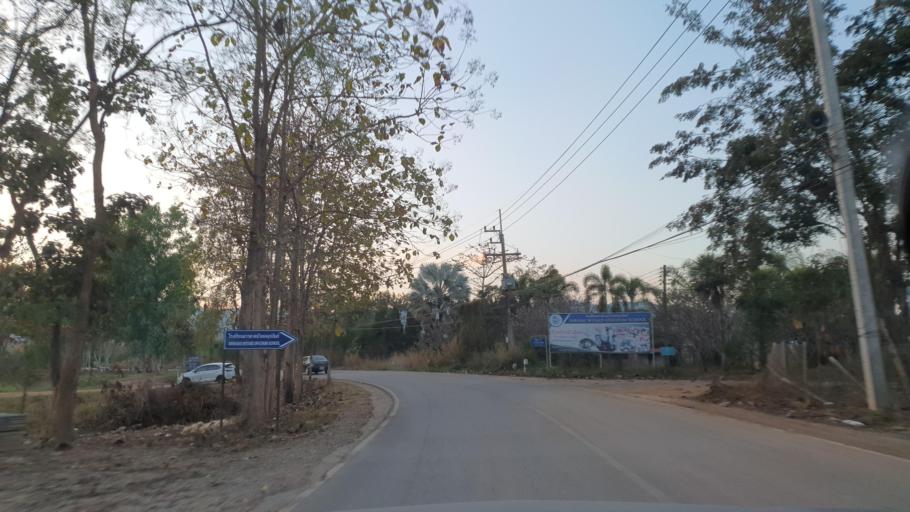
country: TH
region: Chiang Mai
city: Mae Wang
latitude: 18.6384
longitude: 98.7981
